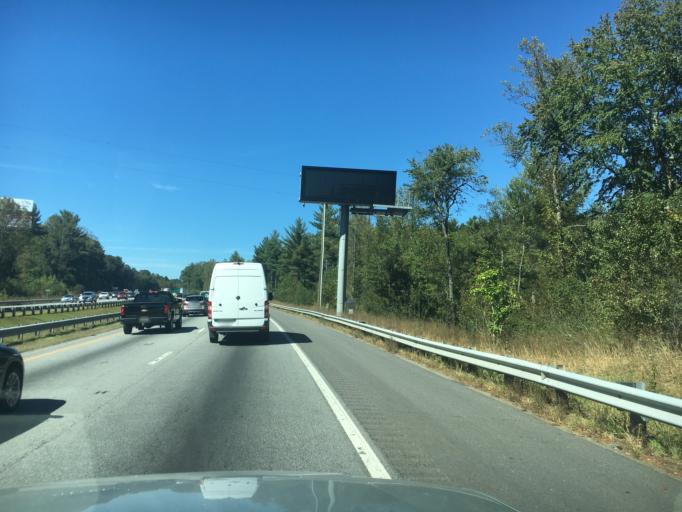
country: US
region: North Carolina
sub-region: Buncombe County
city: Bent Creek
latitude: 35.5185
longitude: -82.5909
